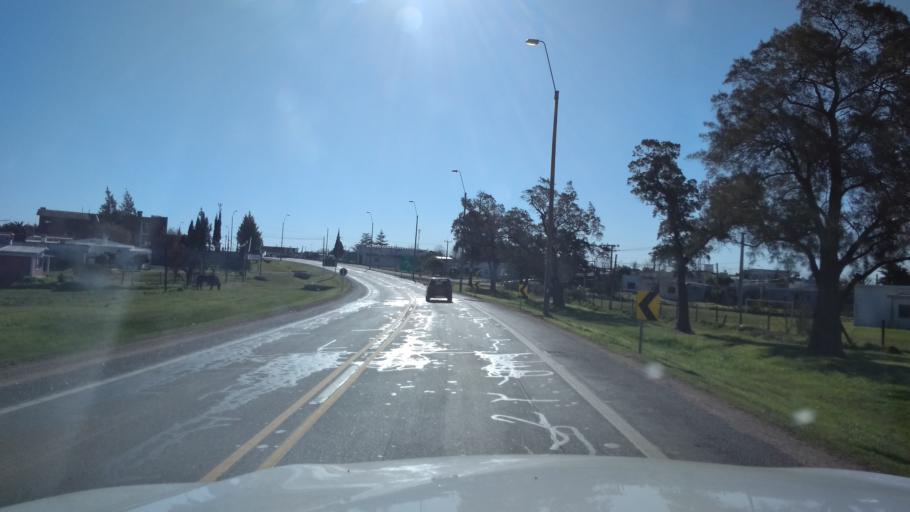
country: UY
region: Canelones
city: San Jacinto
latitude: -34.5492
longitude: -55.8700
